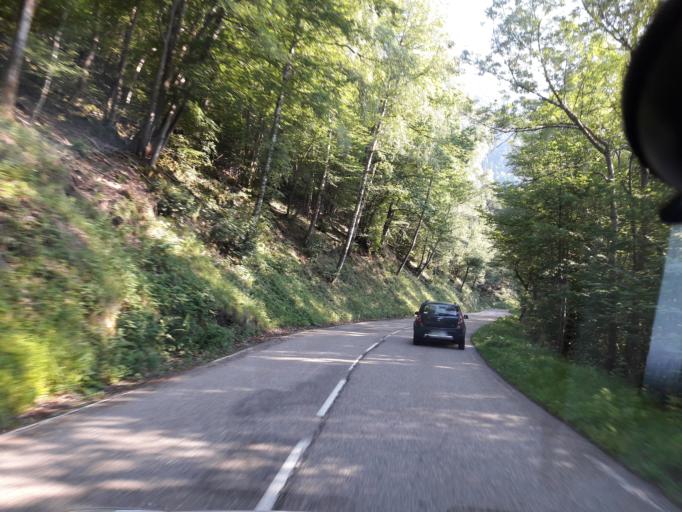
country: FR
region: Rhone-Alpes
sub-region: Departement de l'Isere
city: Vaulnaveys-le-Bas
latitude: 45.0376
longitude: 5.8315
